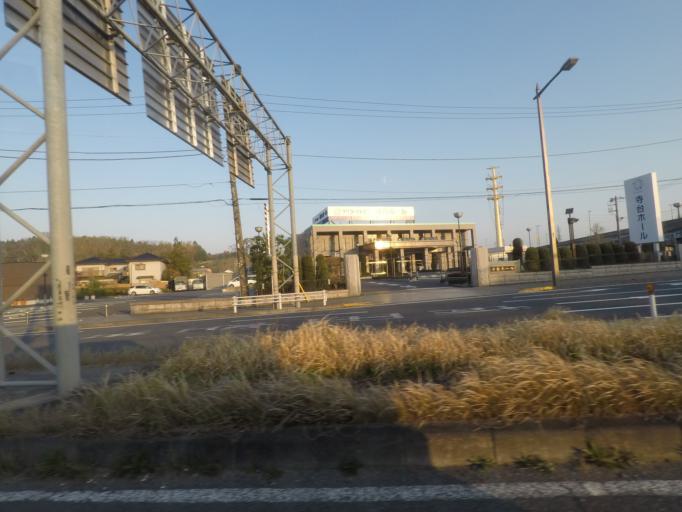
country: JP
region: Chiba
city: Narita
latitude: 35.7874
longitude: 140.3309
